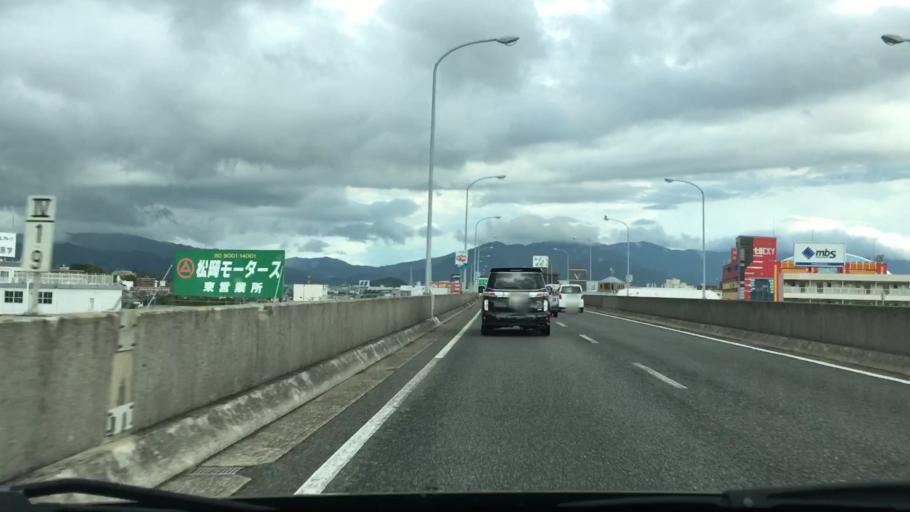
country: JP
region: Fukuoka
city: Fukuoka-shi
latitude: 33.6309
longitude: 130.4382
